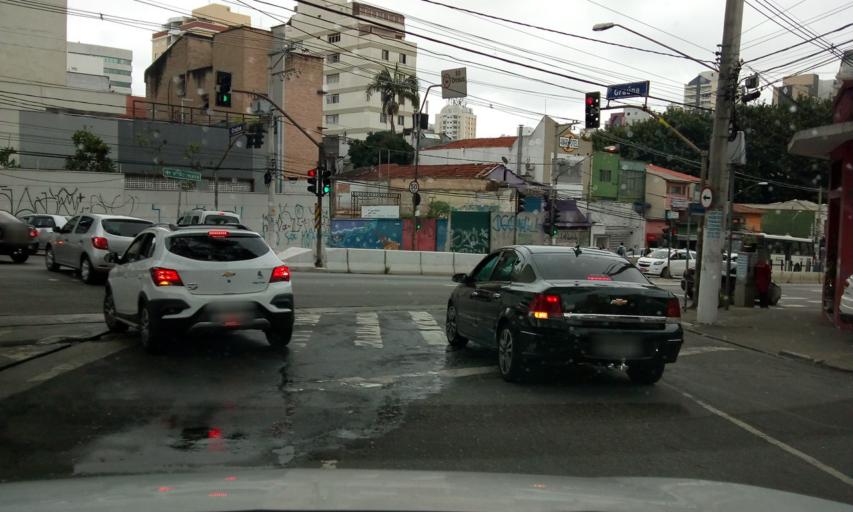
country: BR
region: Sao Paulo
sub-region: Sao Paulo
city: Sao Paulo
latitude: -23.5994
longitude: -46.6737
